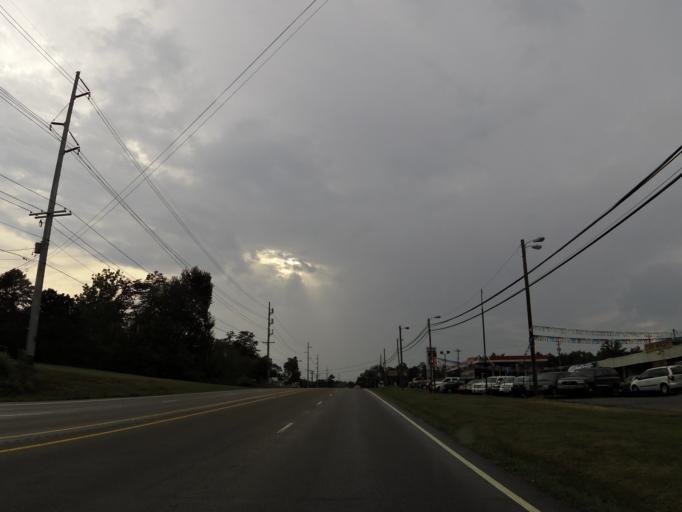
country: US
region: Tennessee
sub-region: Sevier County
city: Seymour
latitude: 35.9003
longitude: -83.8192
